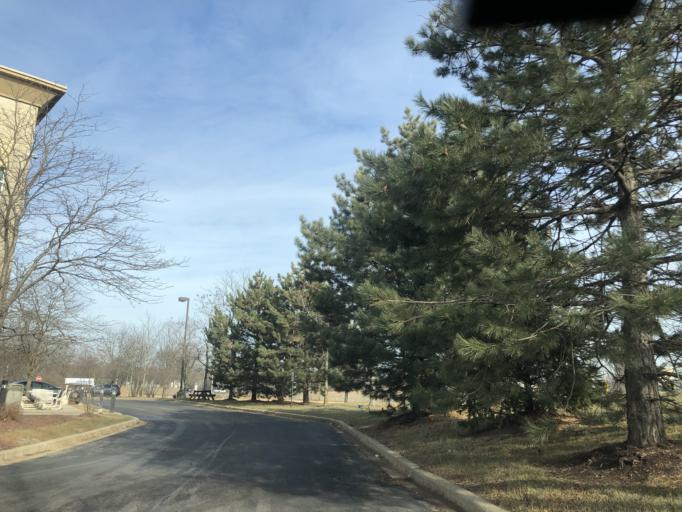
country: US
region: Illinois
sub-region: Cook County
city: Lemont
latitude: 41.7190
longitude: -88.0079
